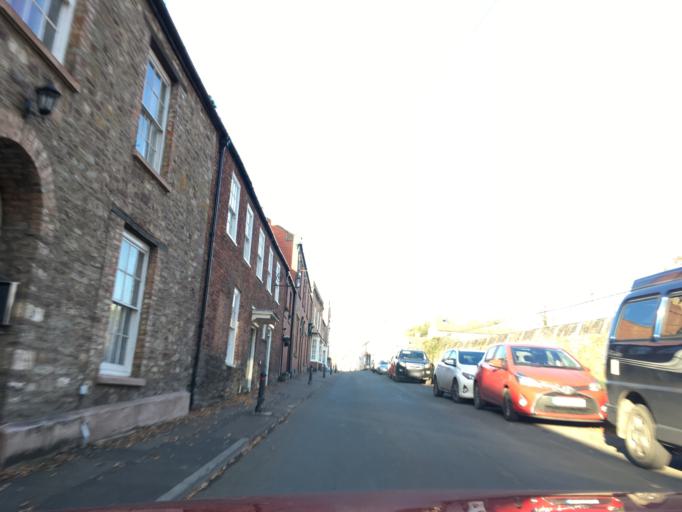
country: GB
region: England
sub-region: Gloucestershire
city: Berkeley
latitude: 51.6891
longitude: -2.4590
